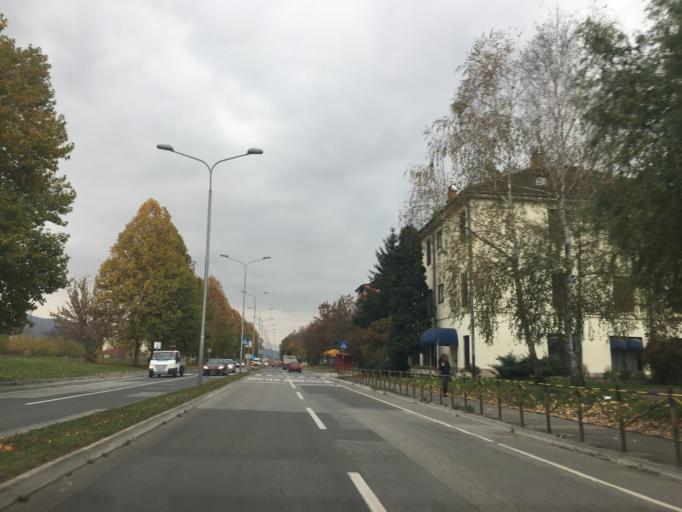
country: RS
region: Central Serbia
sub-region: Raski Okrug
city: Kraljevo
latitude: 43.7256
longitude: 20.7063
